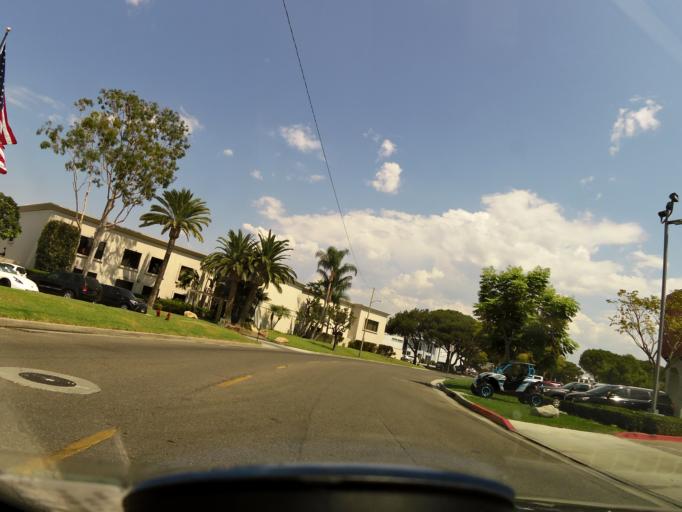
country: US
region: California
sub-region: Orange County
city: Tustin
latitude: 33.7139
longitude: -117.8457
